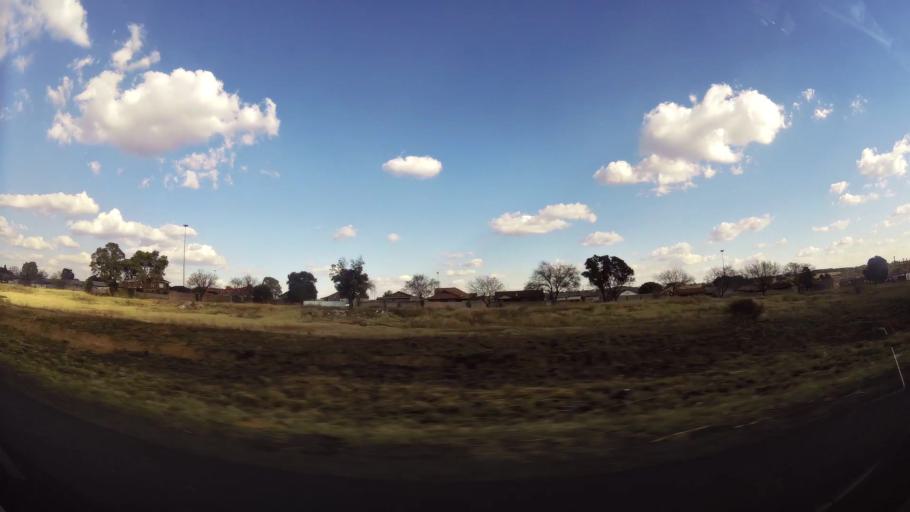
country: ZA
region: Mpumalanga
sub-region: Nkangala District Municipality
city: Witbank
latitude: -25.8822
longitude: 29.1812
